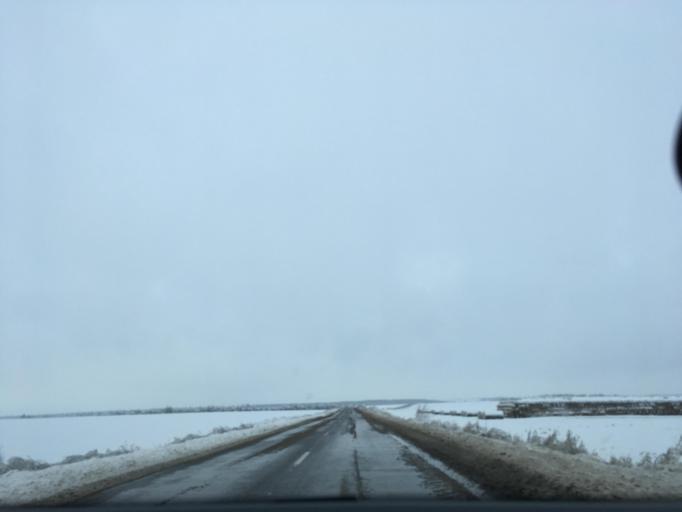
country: RU
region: Voronezj
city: Ol'khovatka
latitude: 50.1323
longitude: 39.1961
